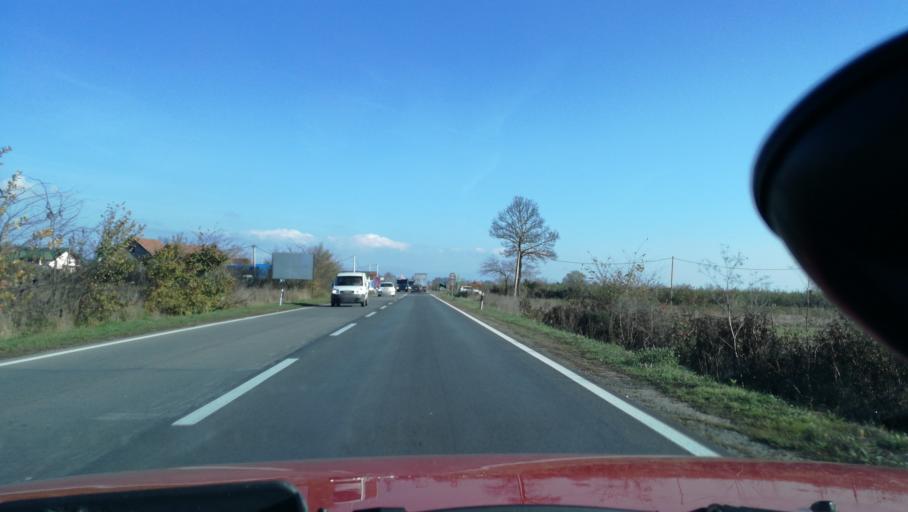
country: RS
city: Prislonica
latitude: 43.8953
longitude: 20.4314
